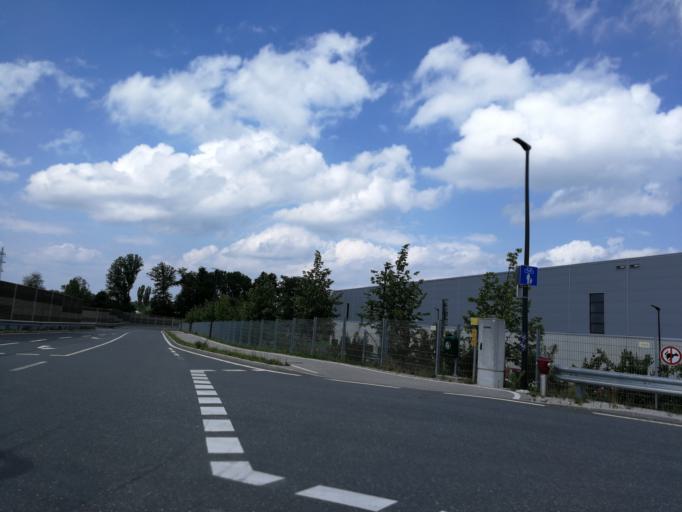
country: DE
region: Bavaria
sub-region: Upper Bavaria
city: Freilassing
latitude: 47.8134
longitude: 12.9865
